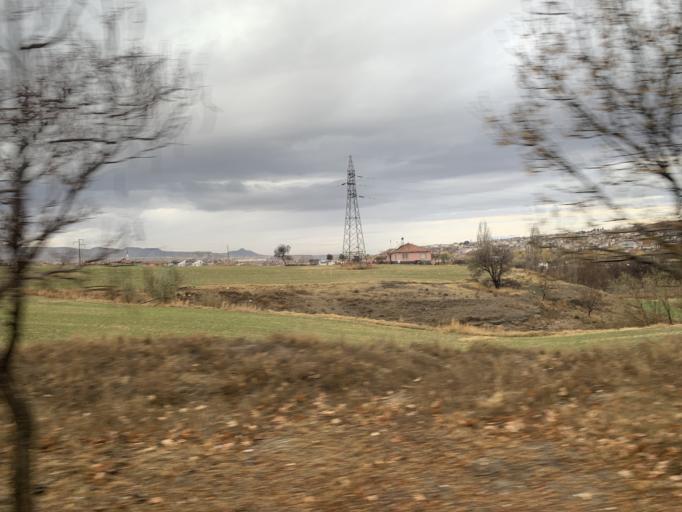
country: TR
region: Nevsehir
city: Avanos
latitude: 38.7138
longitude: 34.8587
